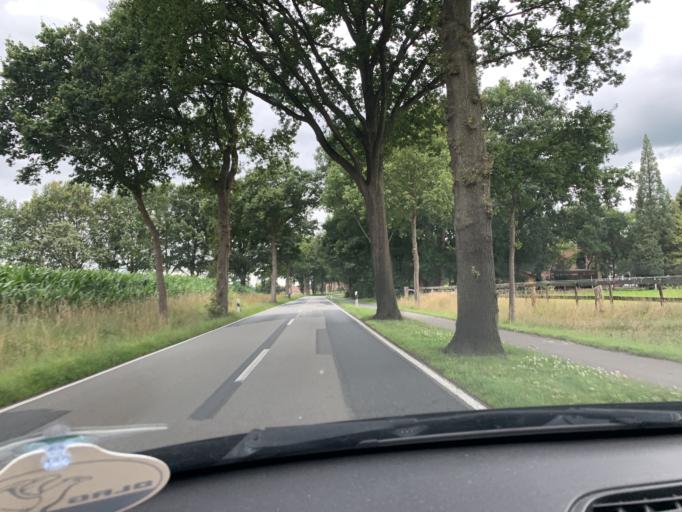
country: DE
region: Lower Saxony
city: Edewecht
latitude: 53.1305
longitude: 7.8914
